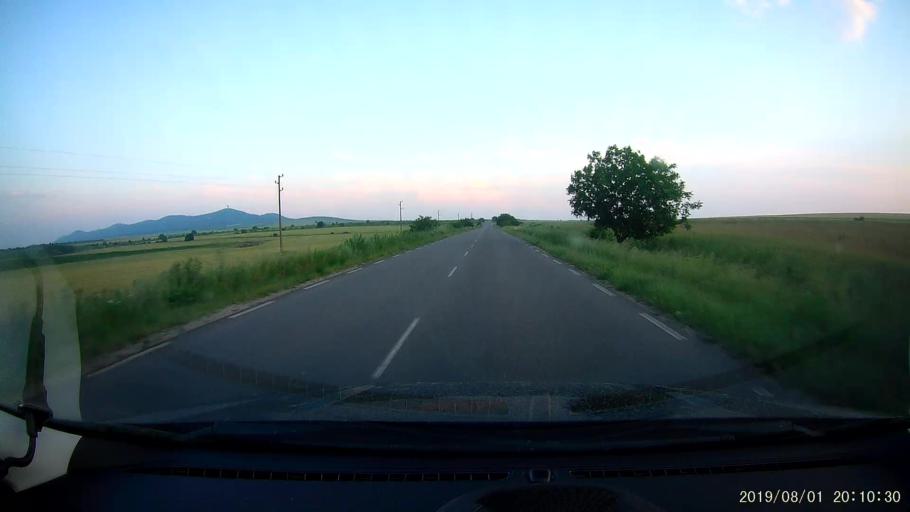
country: BG
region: Yambol
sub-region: Obshtina Yambol
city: Yambol
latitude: 42.4803
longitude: 26.5998
